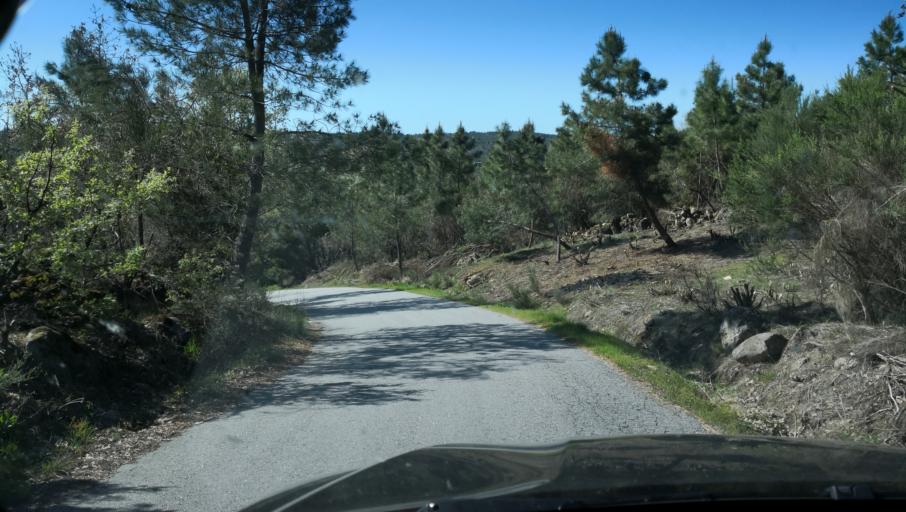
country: PT
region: Vila Real
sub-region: Sabrosa
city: Sabrosa
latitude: 41.2967
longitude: -7.6381
